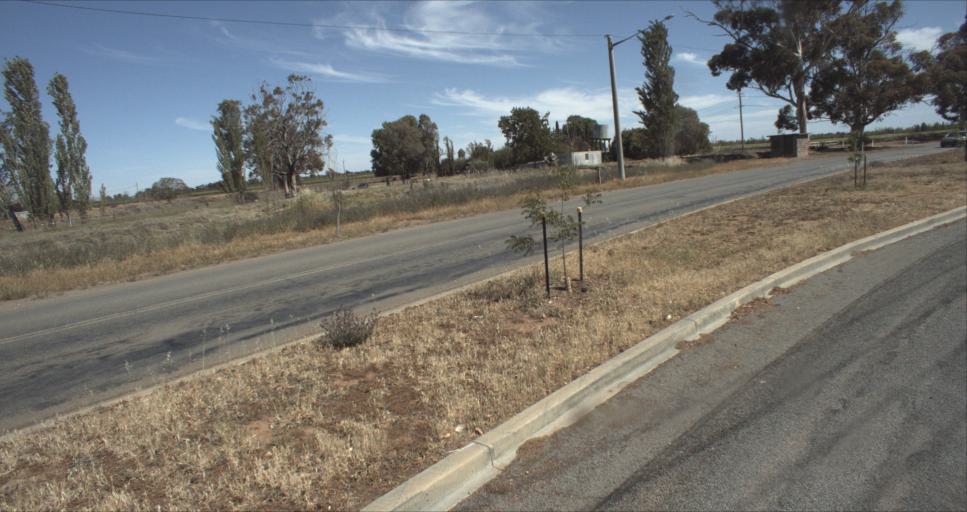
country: AU
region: New South Wales
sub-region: Leeton
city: Leeton
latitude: -34.5523
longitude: 146.3787
